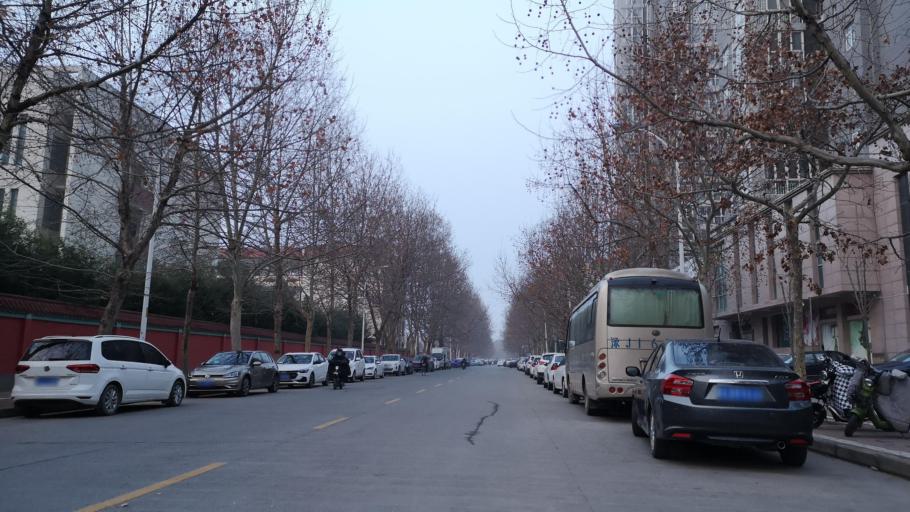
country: CN
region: Henan Sheng
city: Zhongyuanlu
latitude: 35.7535
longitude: 115.0607
